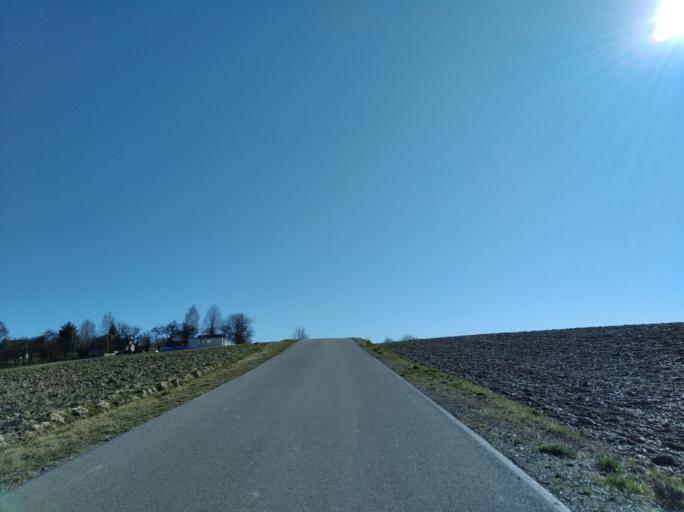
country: PL
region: Subcarpathian Voivodeship
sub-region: Powiat strzyzowski
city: Wisniowa
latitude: 49.9090
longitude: 21.6977
